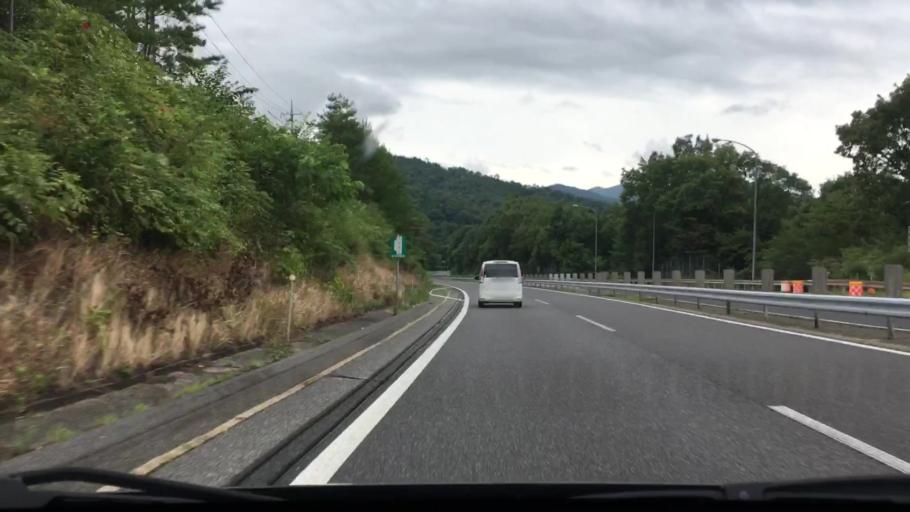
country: JP
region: Hiroshima
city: Hiroshima-shi
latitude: 34.6836
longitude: 132.5617
